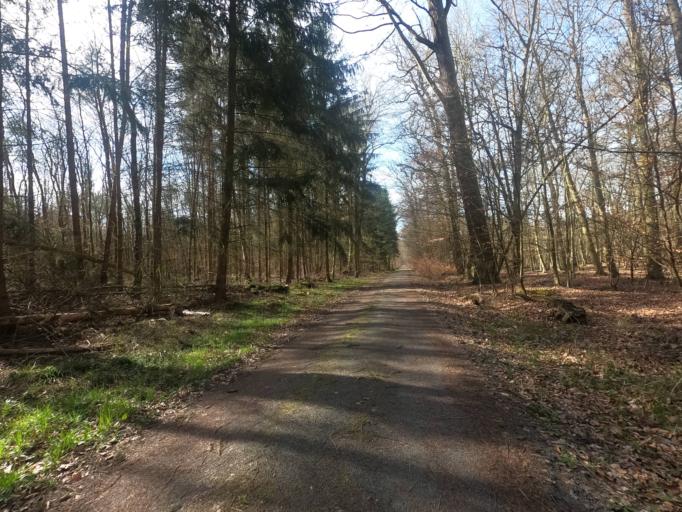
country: DE
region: Hesse
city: Morfelden-Walldorf
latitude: 49.9710
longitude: 8.5264
